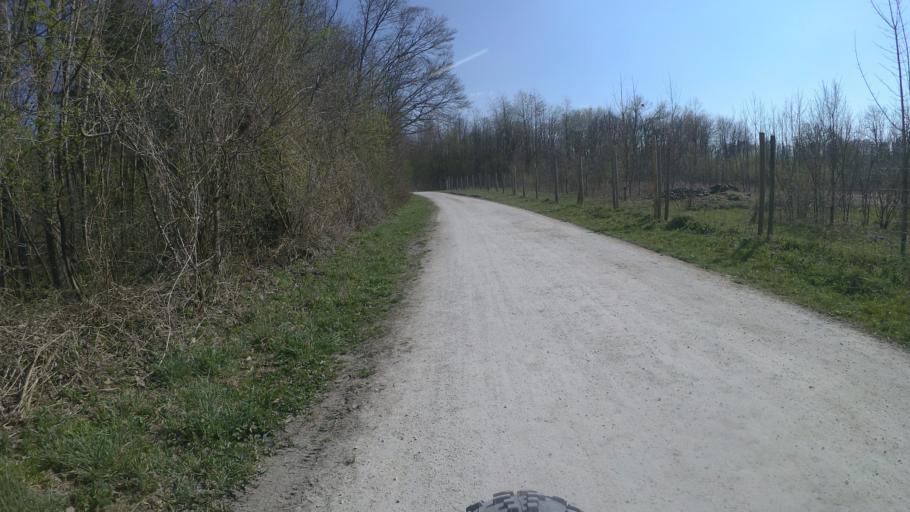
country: DE
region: Bavaria
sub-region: Upper Bavaria
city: Traunreut
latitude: 47.9538
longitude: 12.5831
